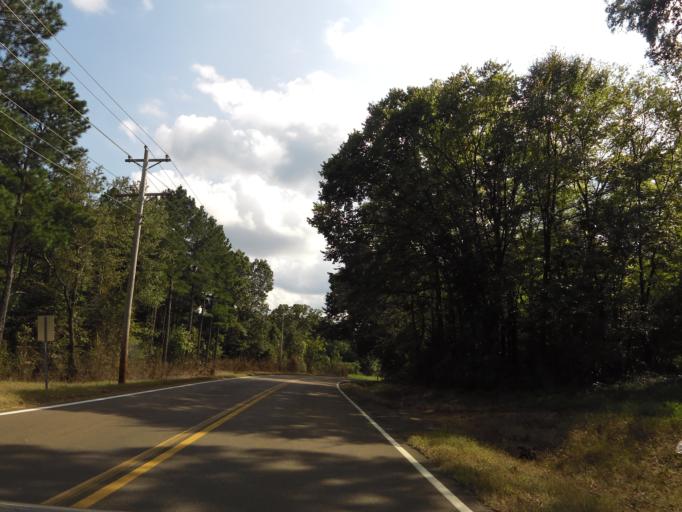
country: US
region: Mississippi
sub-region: Alcorn County
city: Farmington
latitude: 35.0754
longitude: -88.3888
